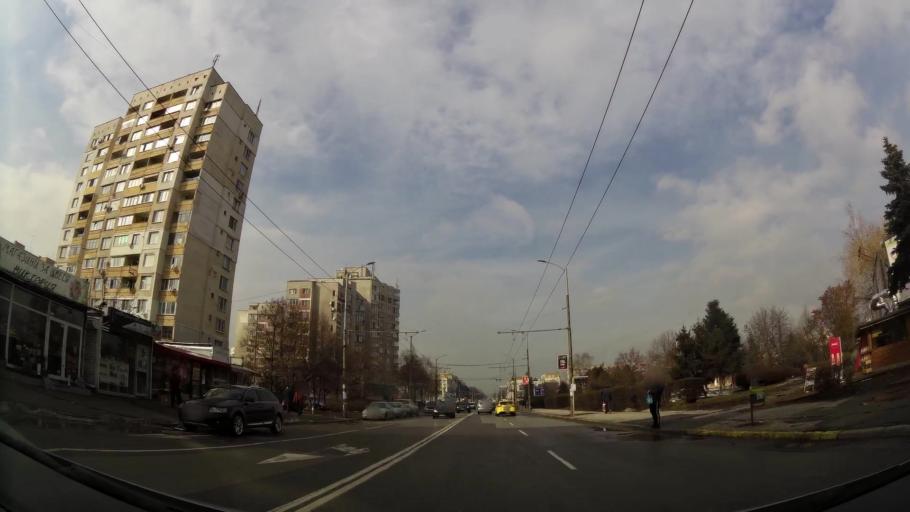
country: BG
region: Sofiya
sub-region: Obshtina Bozhurishte
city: Bozhurishte
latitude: 42.7149
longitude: 23.2531
